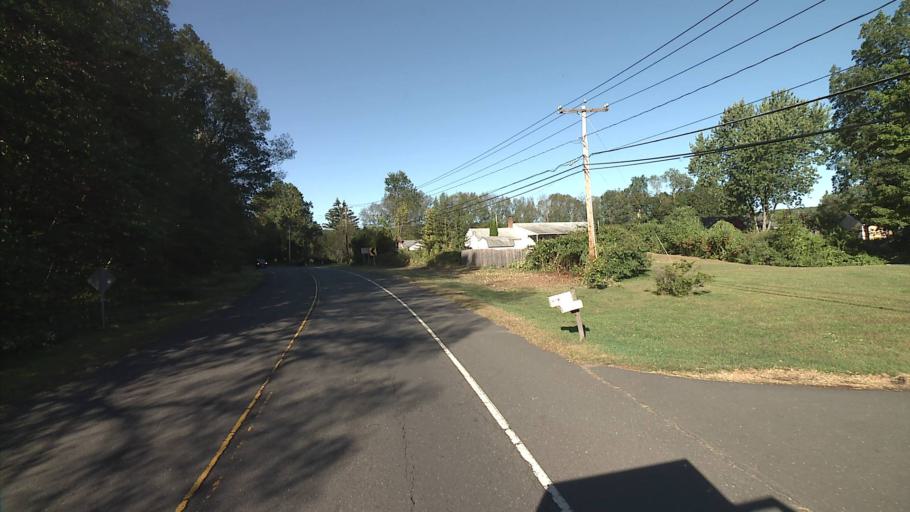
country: US
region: Connecticut
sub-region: New Haven County
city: Cheshire Village
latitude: 41.5111
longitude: -72.9317
